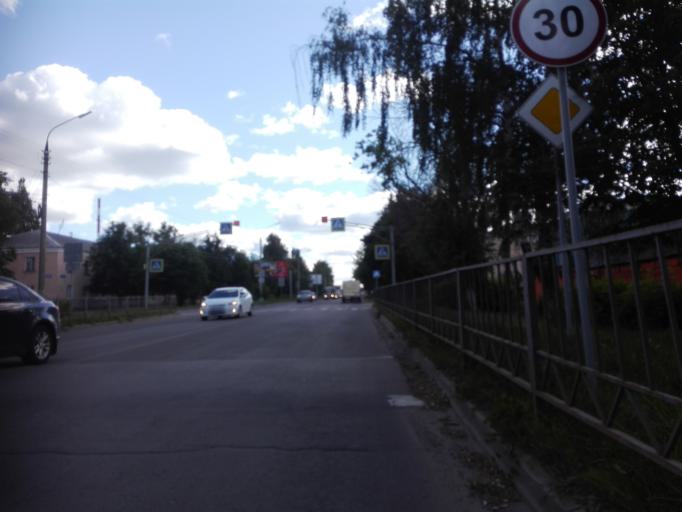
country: RU
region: Orjol
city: Orel
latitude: 52.9492
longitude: 36.0378
